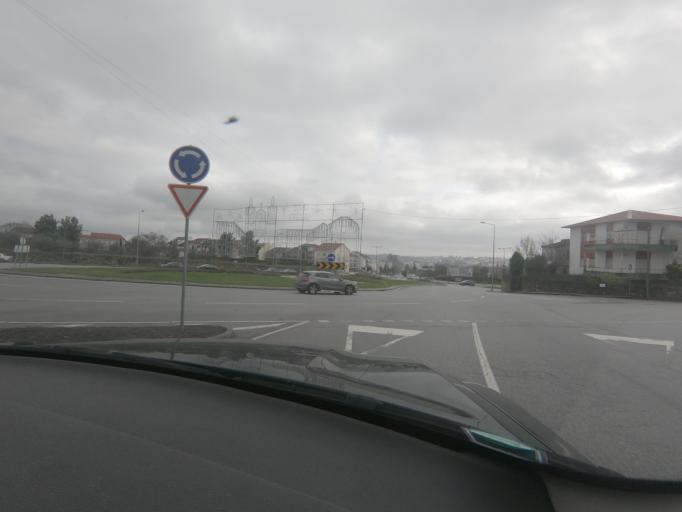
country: PT
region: Viseu
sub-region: Viseu
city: Abraveses
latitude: 40.6764
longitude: -7.9245
